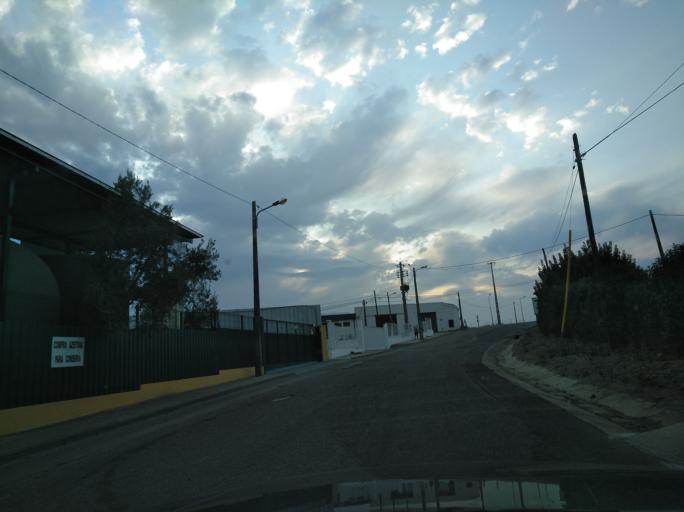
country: PT
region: Portalegre
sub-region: Campo Maior
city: Campo Maior
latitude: 39.0235
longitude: -7.0644
